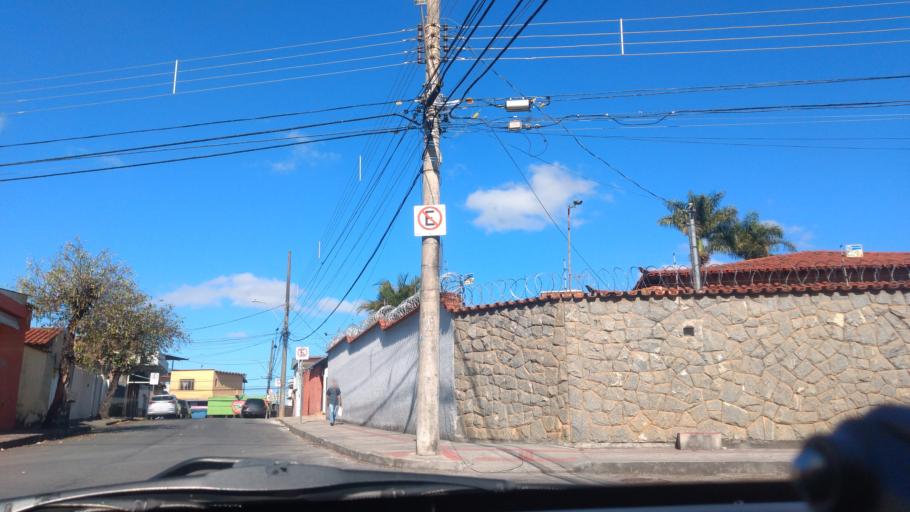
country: BR
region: Minas Gerais
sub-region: Belo Horizonte
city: Belo Horizonte
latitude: -19.8408
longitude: -43.9491
